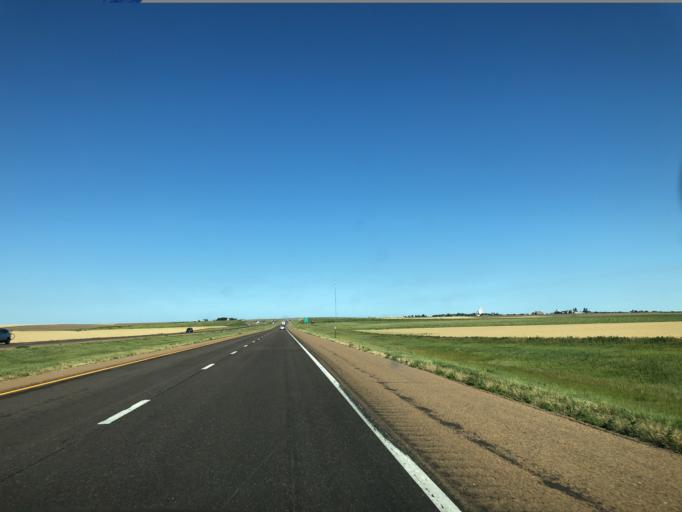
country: US
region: Kansas
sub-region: Sherman County
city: Goodland
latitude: 39.3301
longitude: -101.5123
